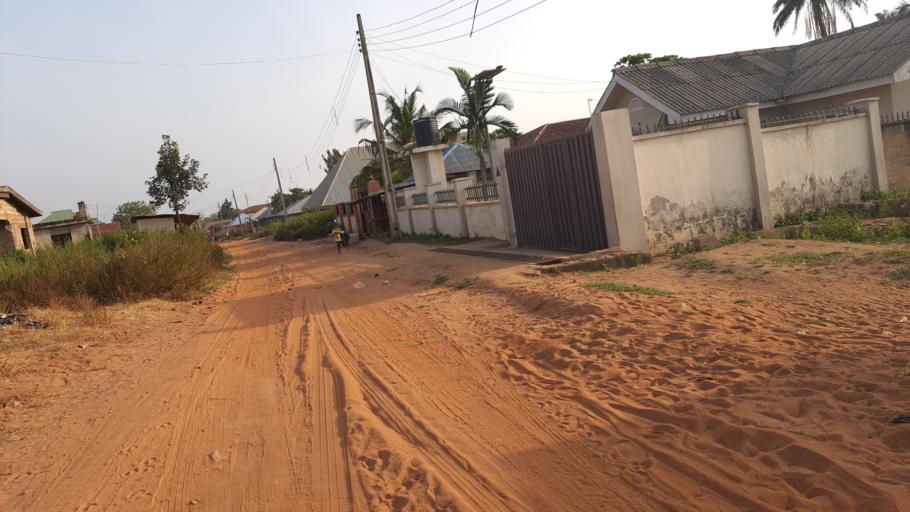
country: NG
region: Osun
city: Iwo
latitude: 7.6239
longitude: 4.1585
